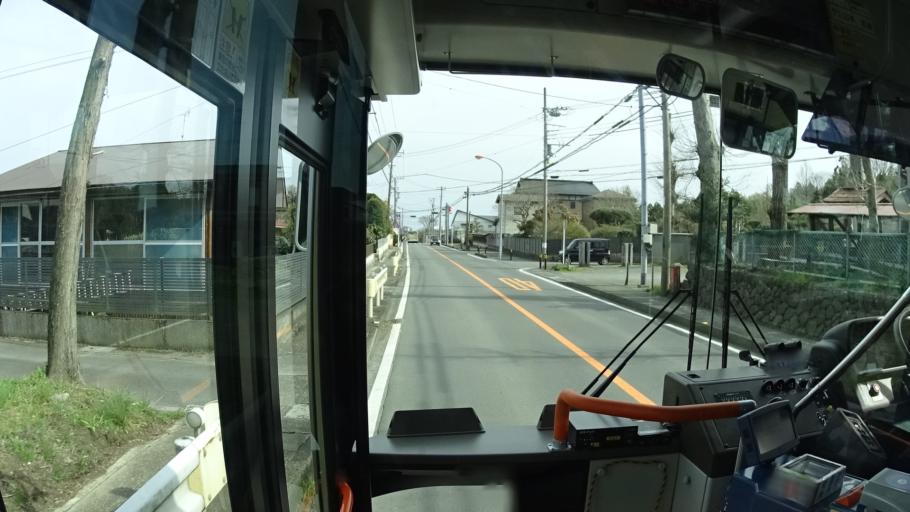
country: JP
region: Kanagawa
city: Zama
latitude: 35.5114
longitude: 139.3027
